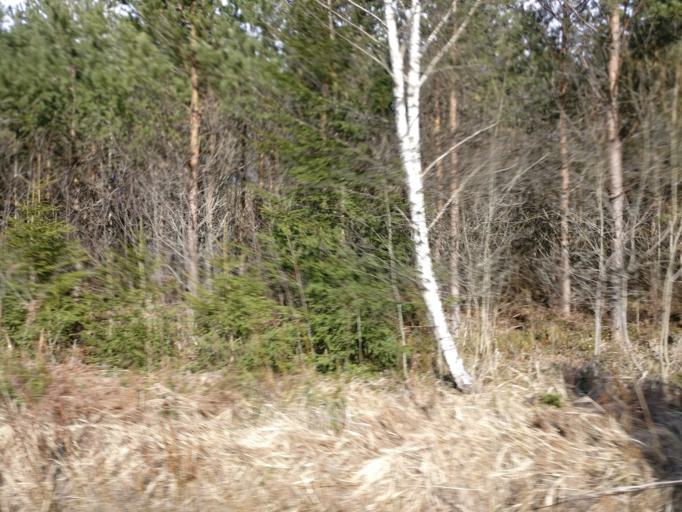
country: FI
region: Uusimaa
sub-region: Helsinki
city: Karjalohja
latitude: 60.3132
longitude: 23.7373
